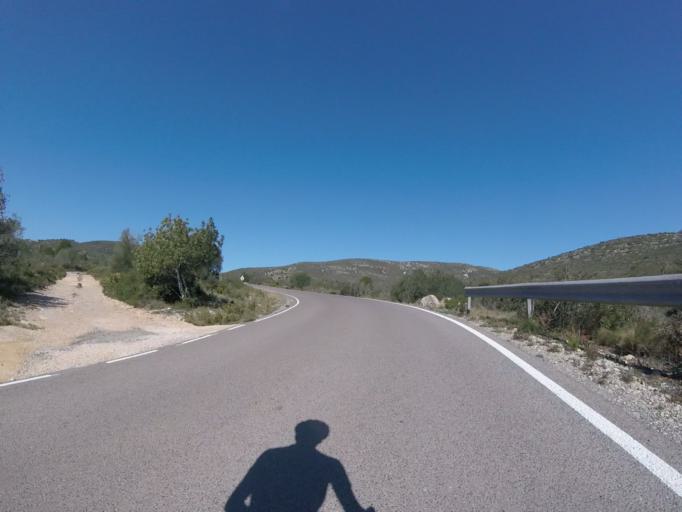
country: ES
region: Valencia
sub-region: Provincia de Castello
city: Santa Magdalena de Pulpis
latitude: 40.3796
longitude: 0.2687
